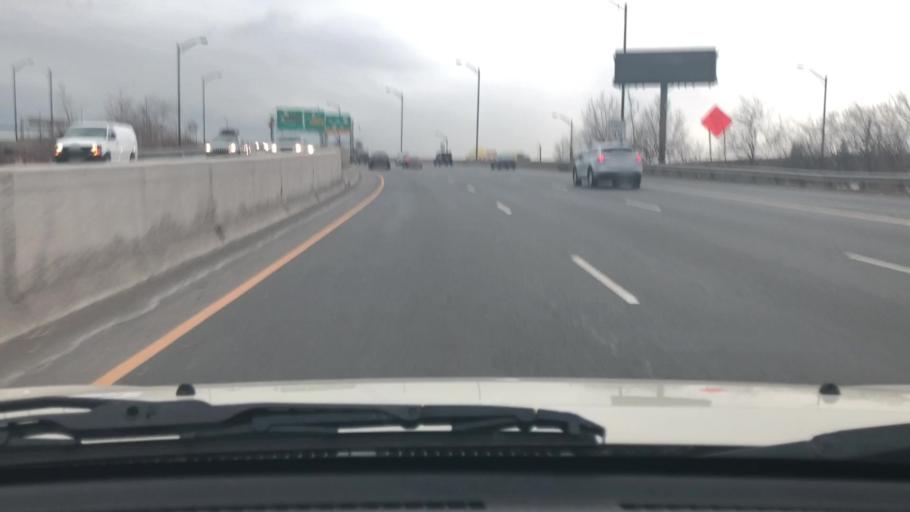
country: US
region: New Jersey
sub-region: Essex County
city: Newark
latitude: 40.7179
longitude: -74.1826
